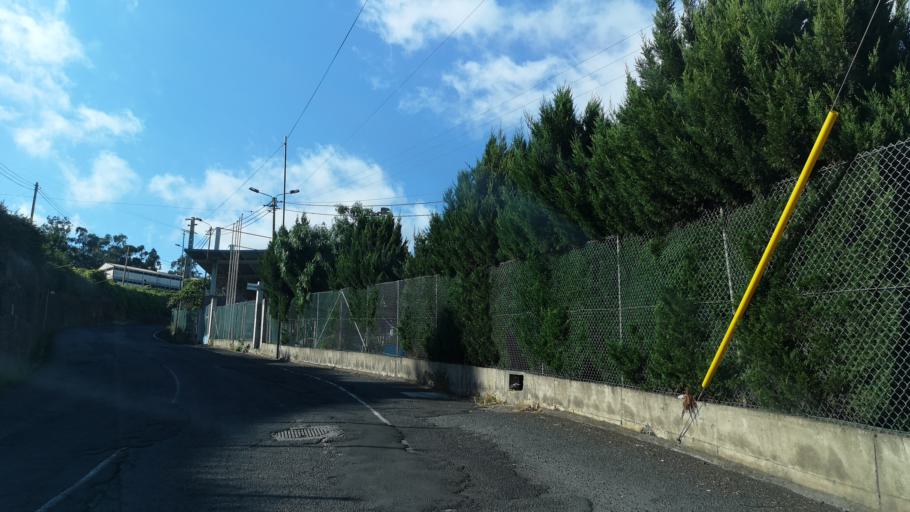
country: PT
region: Madeira
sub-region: Santa Cruz
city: Camacha
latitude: 32.6599
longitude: -16.8357
